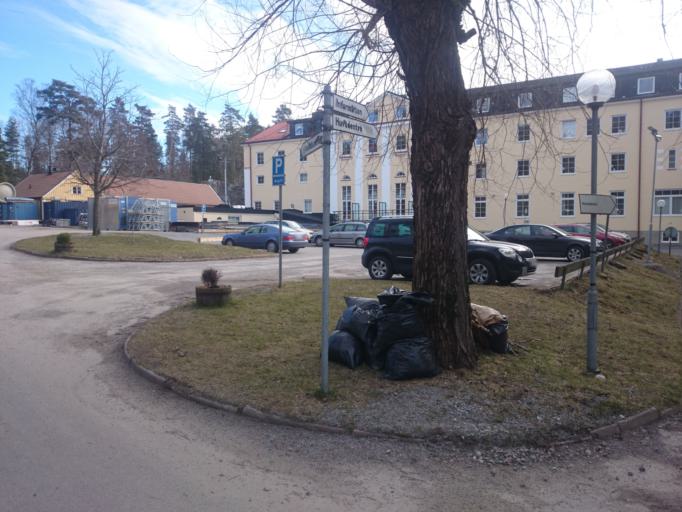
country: SE
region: Stockholm
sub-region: Botkyrka Kommun
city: Tumba
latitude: 59.2015
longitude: 17.8029
